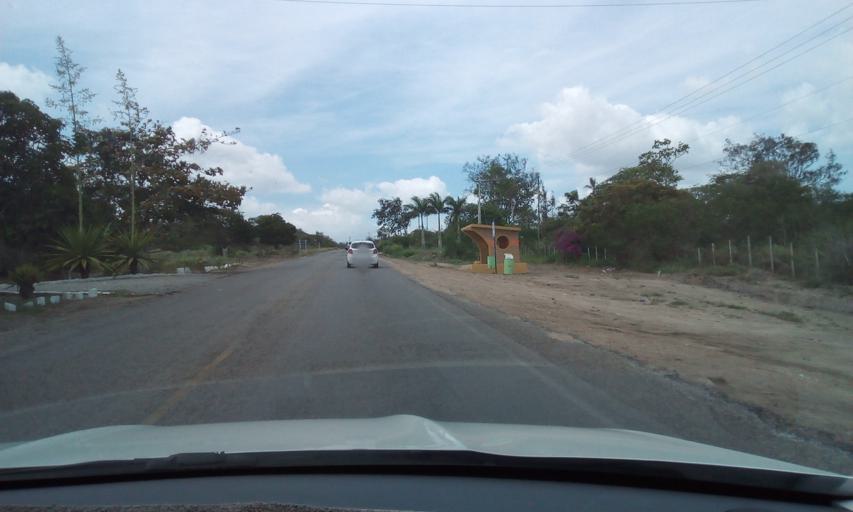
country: BR
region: Pernambuco
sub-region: Bezerros
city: Bezerros
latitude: -8.2802
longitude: -35.7424
